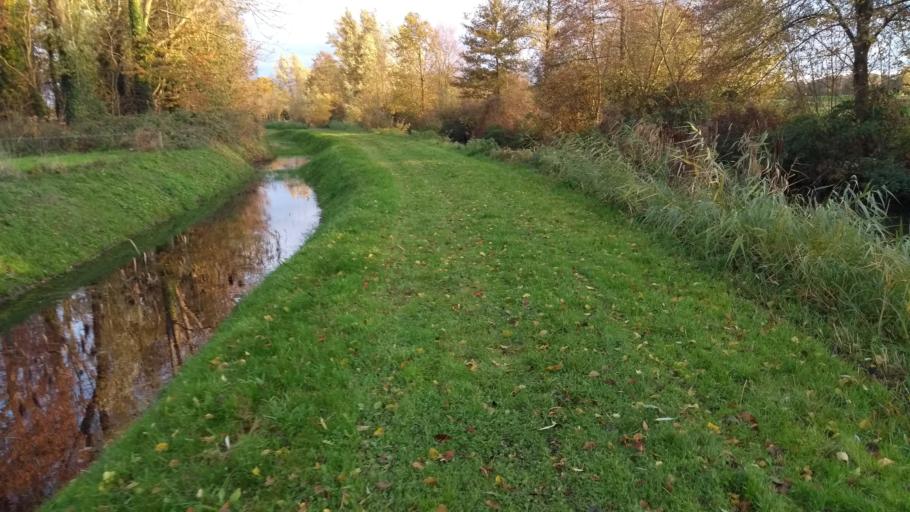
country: NL
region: Overijssel
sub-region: Gemeente Borne
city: Borne
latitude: 52.3351
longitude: 6.7409
